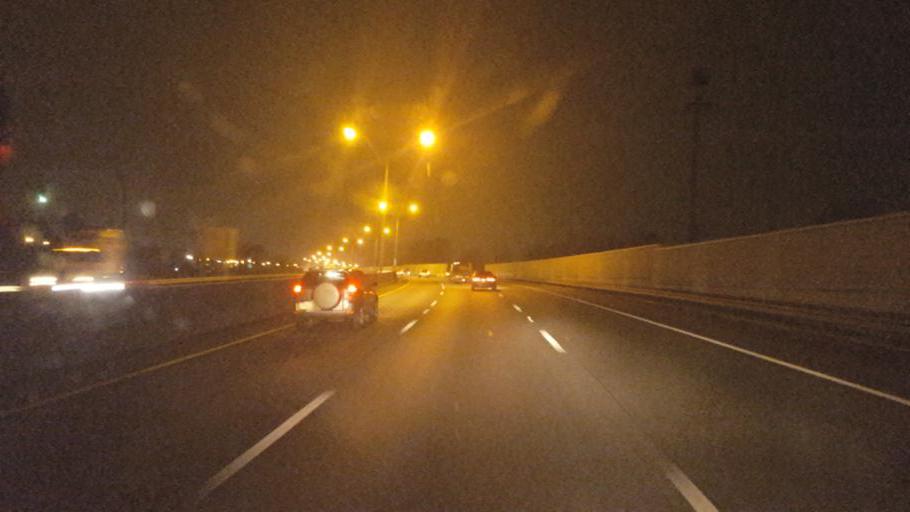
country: US
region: Ohio
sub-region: Franklin County
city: Columbus
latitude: 40.0087
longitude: -82.9861
